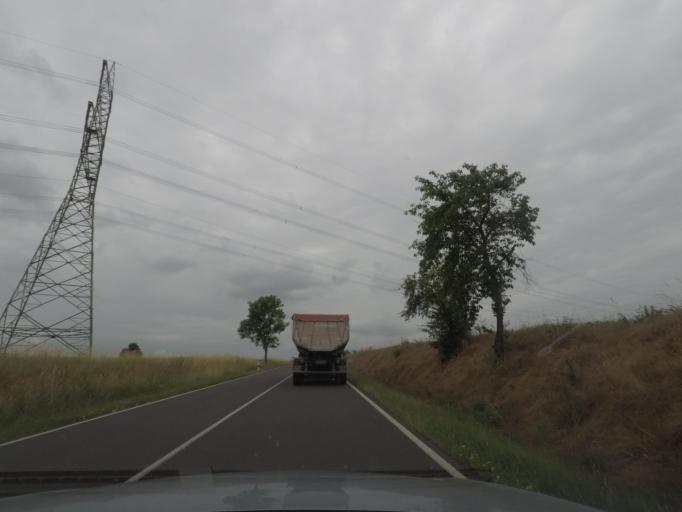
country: DE
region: Saxony-Anhalt
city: Suplingen
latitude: 52.2285
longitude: 11.3117
